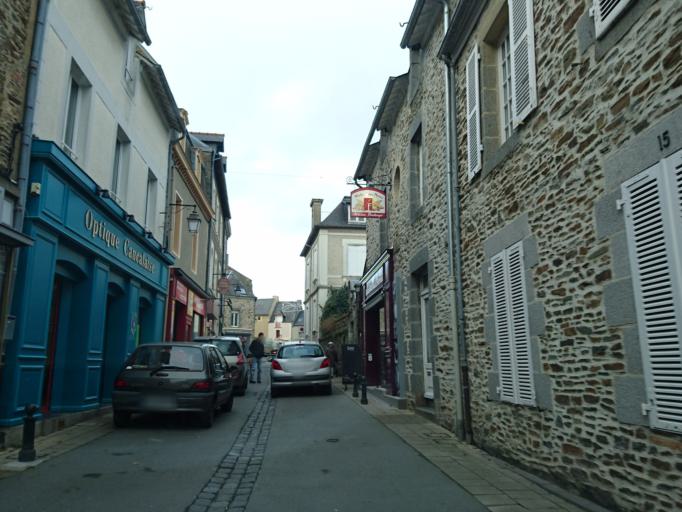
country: FR
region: Brittany
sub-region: Departement d'Ille-et-Vilaine
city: Cancale
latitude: 48.6765
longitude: -1.8514
